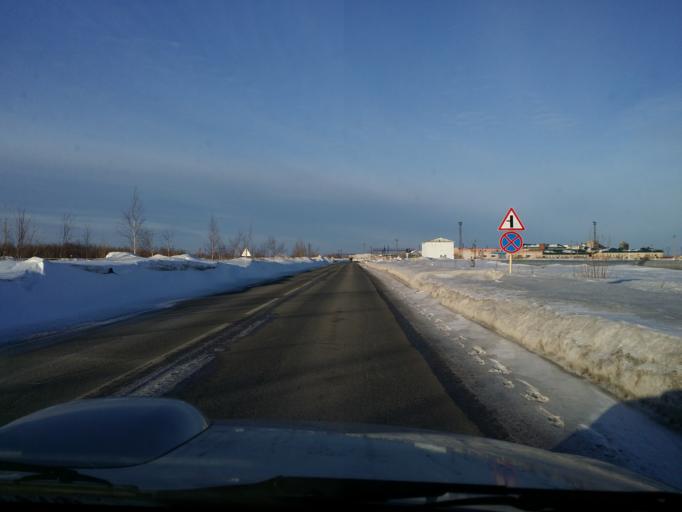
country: RU
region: Khanty-Mansiyskiy Avtonomnyy Okrug
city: Izluchinsk
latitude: 60.9782
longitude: 76.9007
